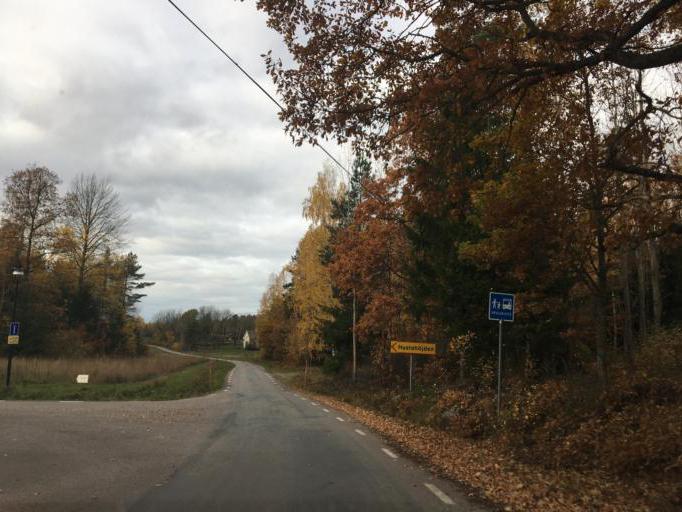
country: SE
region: Vaestmanland
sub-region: Vasteras
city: Vasteras
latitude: 59.5659
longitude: 16.4381
